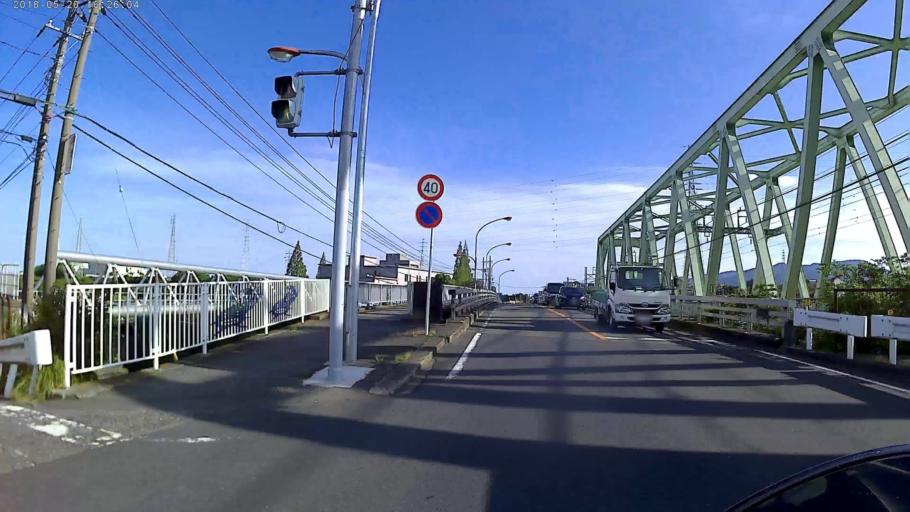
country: JP
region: Kanagawa
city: Odawara
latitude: 35.2802
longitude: 139.1553
